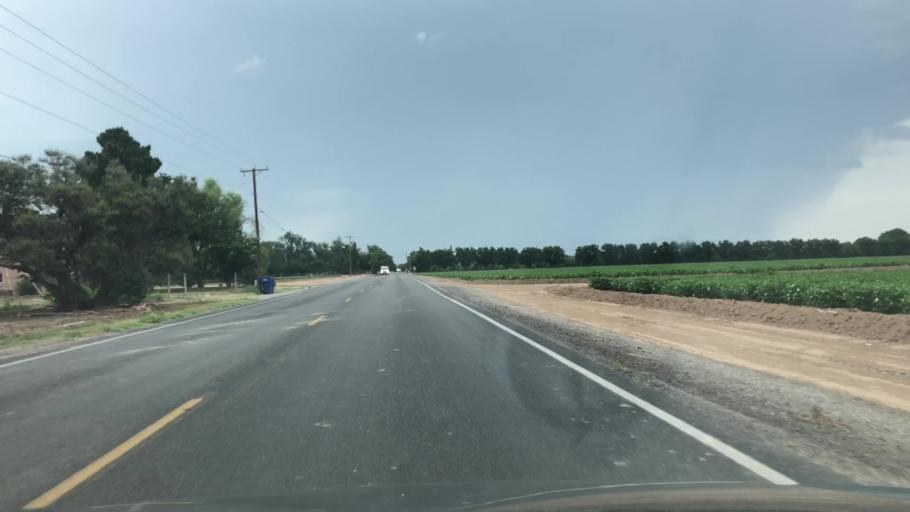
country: US
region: New Mexico
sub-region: Dona Ana County
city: La Union
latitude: 31.9769
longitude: -106.6515
